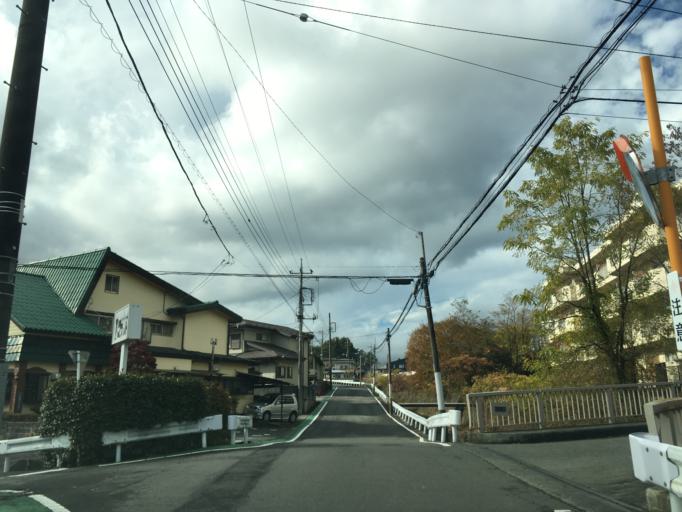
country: JP
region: Yamanashi
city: Fujikawaguchiko
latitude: 35.4860
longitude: 138.7843
